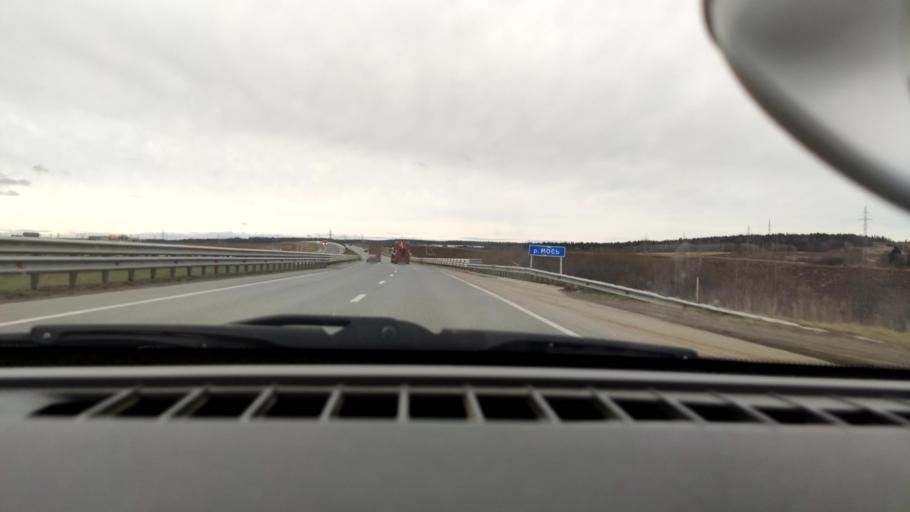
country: RU
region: Perm
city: Ferma
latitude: 57.9315
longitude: 56.3421
